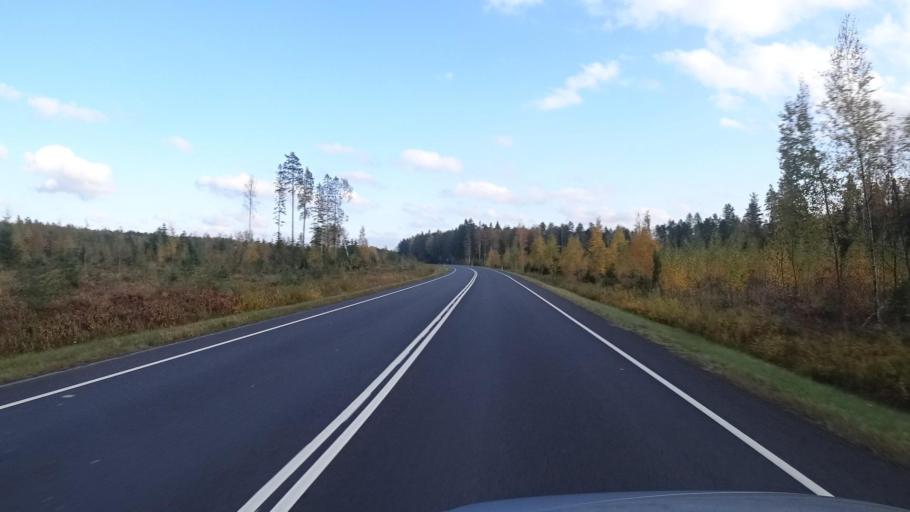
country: FI
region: Satakunta
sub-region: Rauma
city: Eura
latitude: 61.1088
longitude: 22.2123
